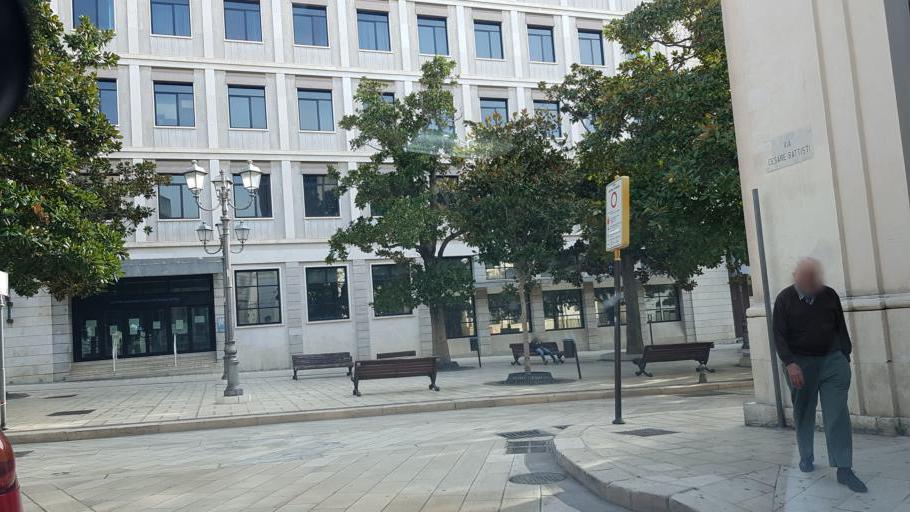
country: IT
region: Apulia
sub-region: Provincia di Brindisi
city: Brindisi
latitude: 40.6375
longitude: 17.9452
